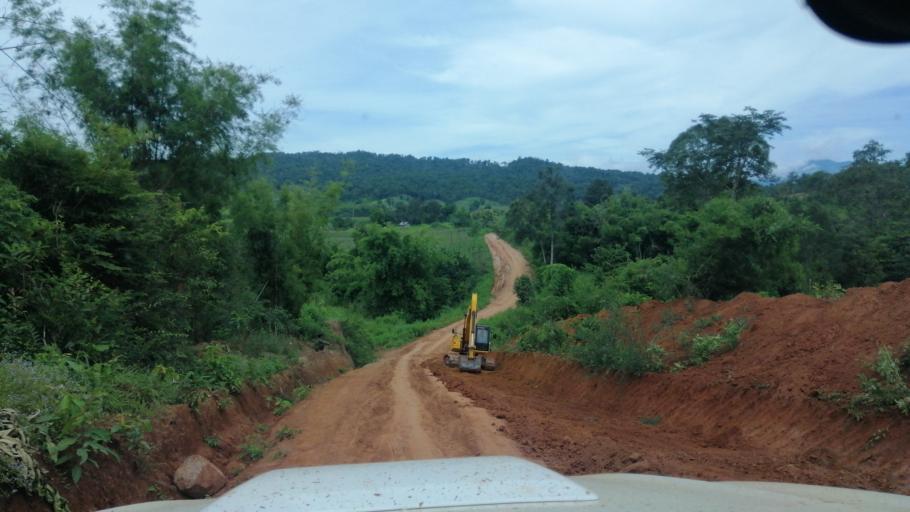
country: TH
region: Loei
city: Na Haeo
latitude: 17.5822
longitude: 101.1443
